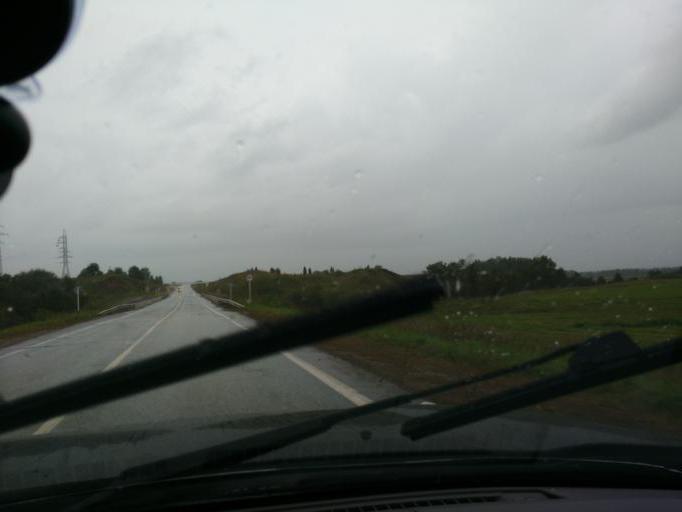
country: RU
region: Perm
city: Barda
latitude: 57.0900
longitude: 55.5375
